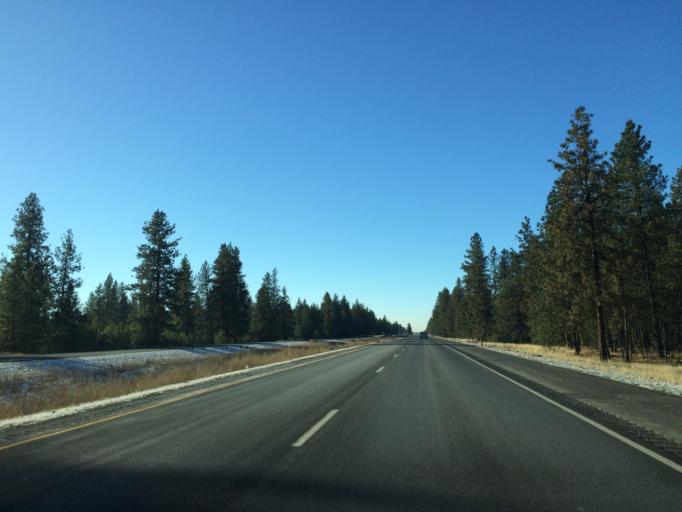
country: US
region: Washington
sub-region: Spokane County
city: Medical Lake
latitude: 47.4824
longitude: -117.7234
